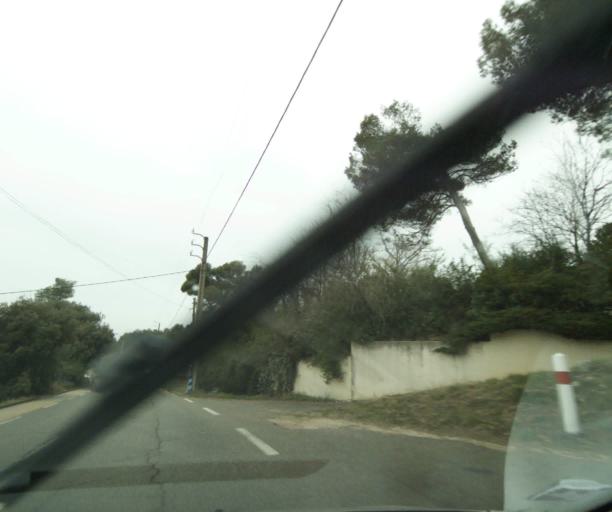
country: FR
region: Provence-Alpes-Cote d'Azur
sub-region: Departement des Bouches-du-Rhone
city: Rognes
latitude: 43.6624
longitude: 5.3686
